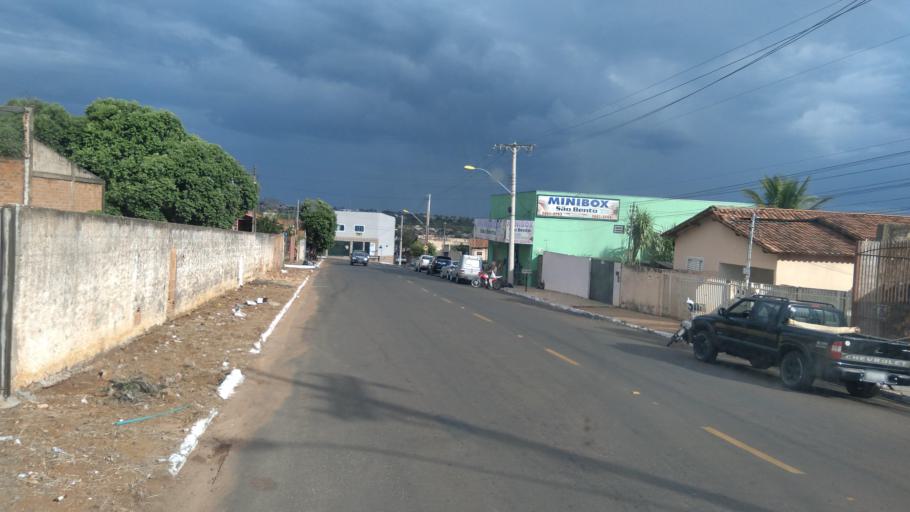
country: BR
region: Goias
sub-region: Mineiros
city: Mineiros
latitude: -17.5671
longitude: -52.5616
